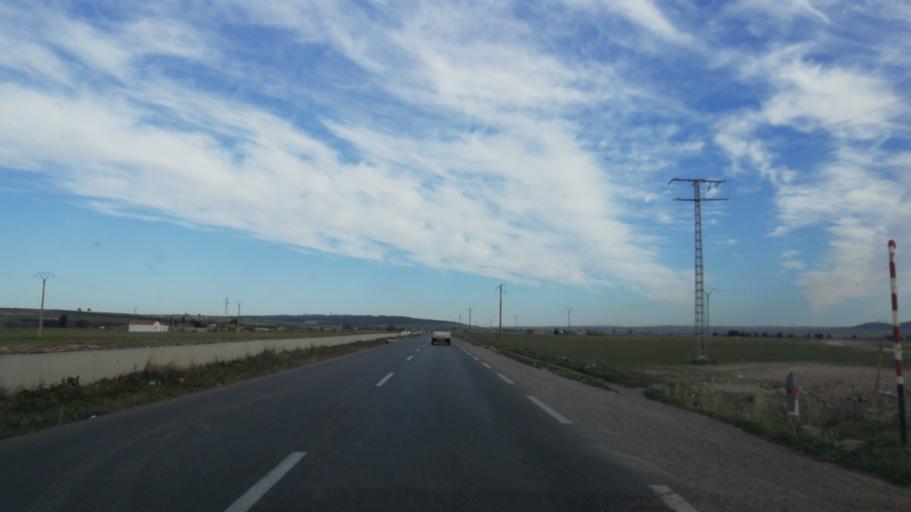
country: DZ
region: Sidi Bel Abbes
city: Sidi Bel Abbes
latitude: 35.1783
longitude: -0.4935
